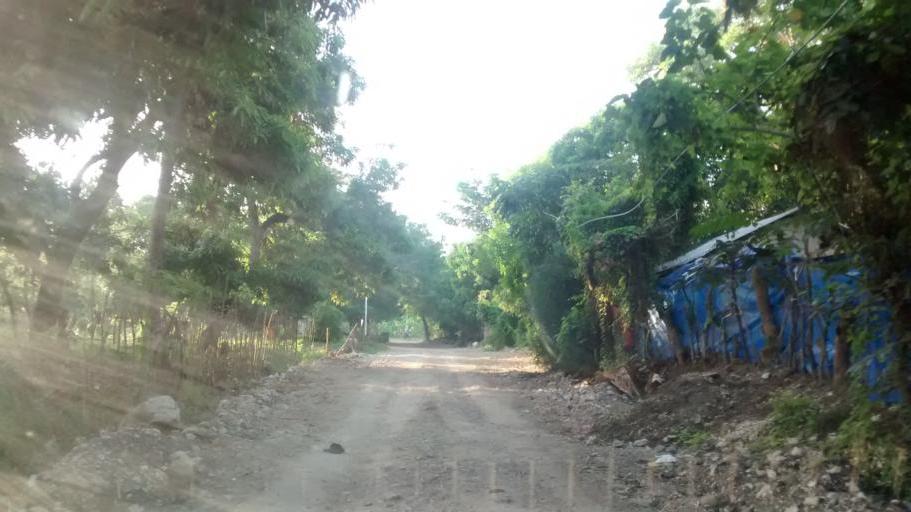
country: HT
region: Ouest
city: Grangwav
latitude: 18.4245
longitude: -72.7830
